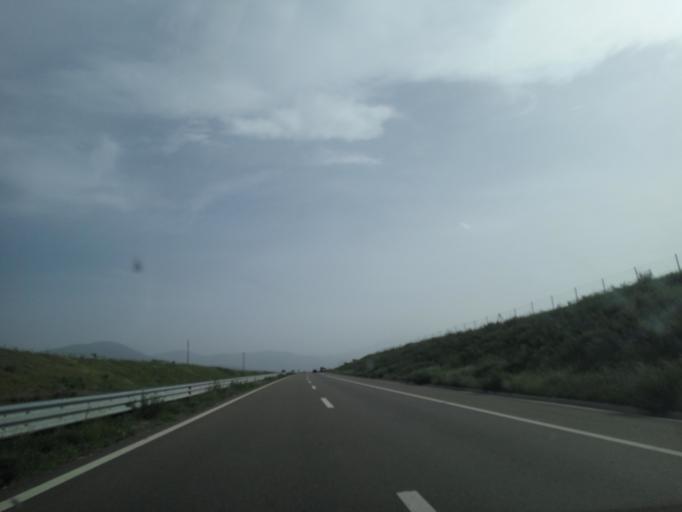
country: XK
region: Prizren
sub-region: Komuna e Therandes
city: Leshan
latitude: 42.2846
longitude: 20.7561
